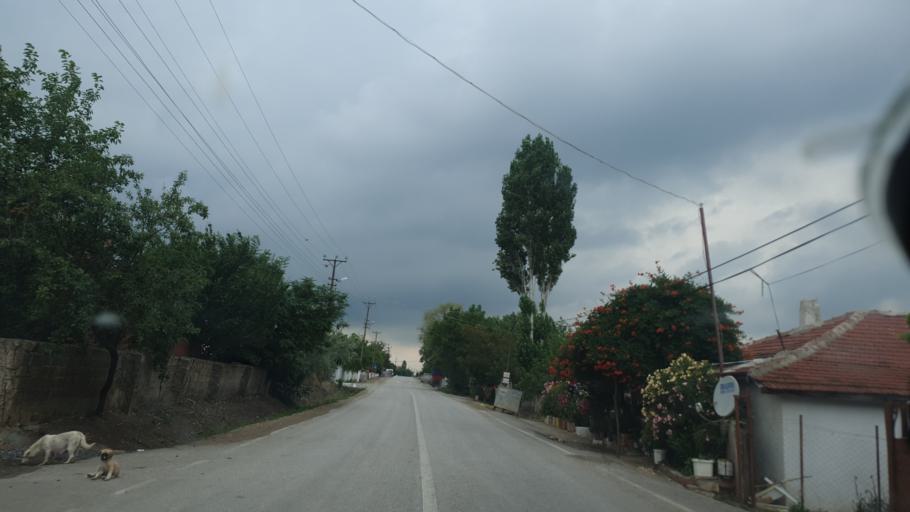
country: TR
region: Tekirdag
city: Hayrabolu
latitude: 41.2199
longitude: 26.9836
